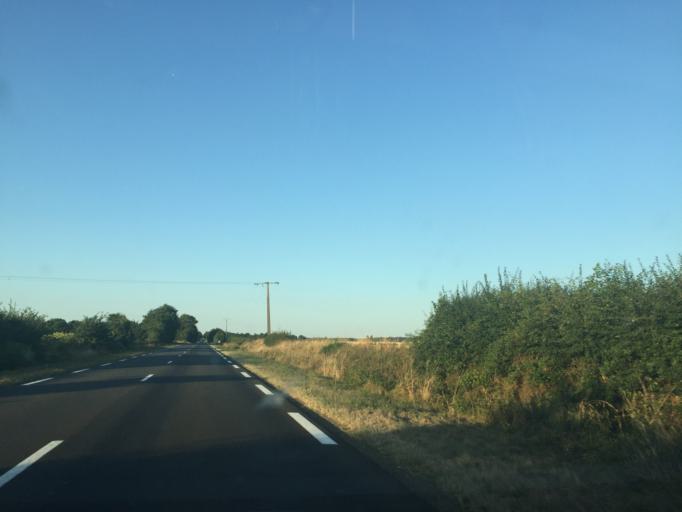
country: FR
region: Poitou-Charentes
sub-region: Departement de la Vienne
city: Rouille
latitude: 46.3931
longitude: 0.0601
